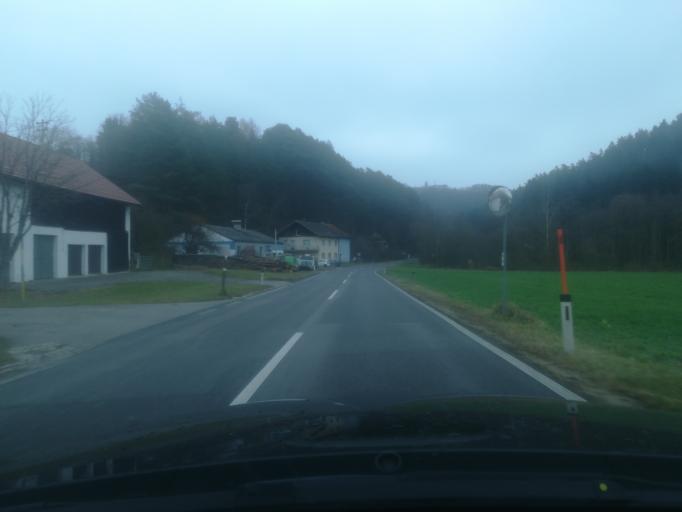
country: AT
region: Upper Austria
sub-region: Politischer Bezirk Perg
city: Perg
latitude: 48.3212
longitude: 14.5662
